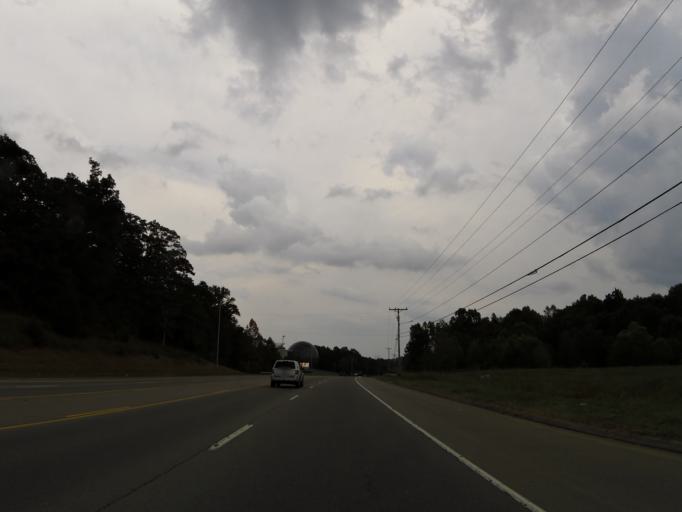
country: US
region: Tennessee
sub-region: Dickson County
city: Dickson
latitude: 36.0478
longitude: -87.3621
